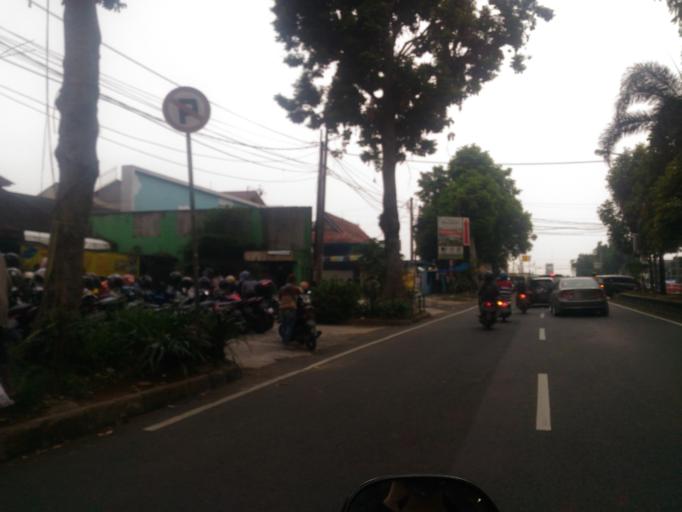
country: ID
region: West Java
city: Bogor
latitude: -6.6222
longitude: 106.8180
